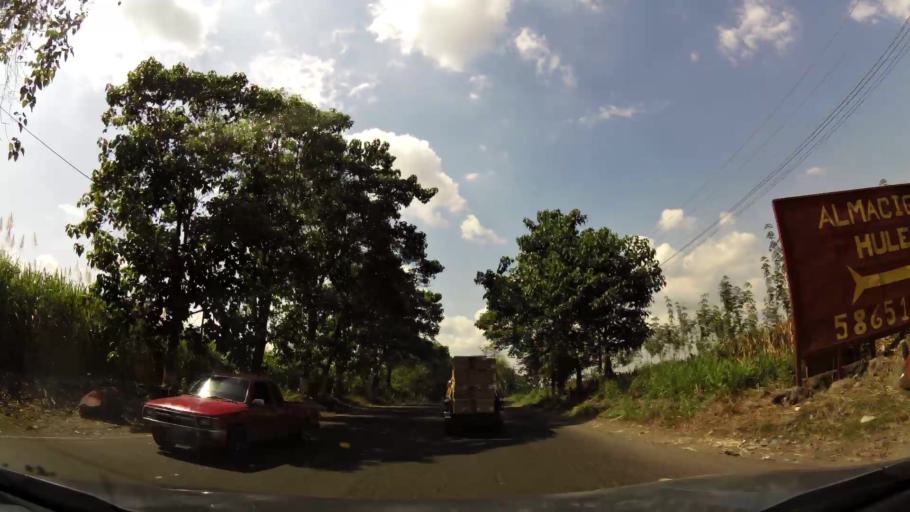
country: GT
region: Suchitepeque
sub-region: Municipio de Cuyotenango
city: Cuyotenango
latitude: 14.5435
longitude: -91.5471
